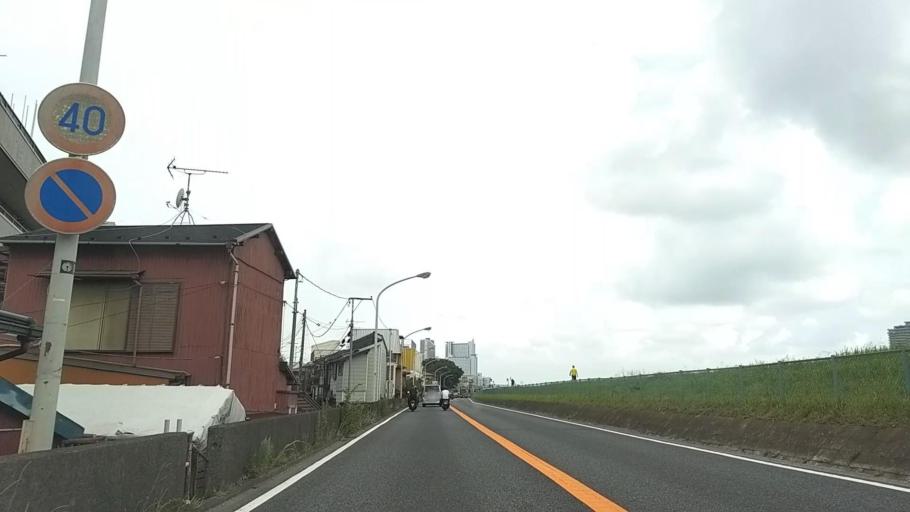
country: JP
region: Kanagawa
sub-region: Kawasaki-shi
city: Kawasaki
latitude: 35.5589
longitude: 139.6814
